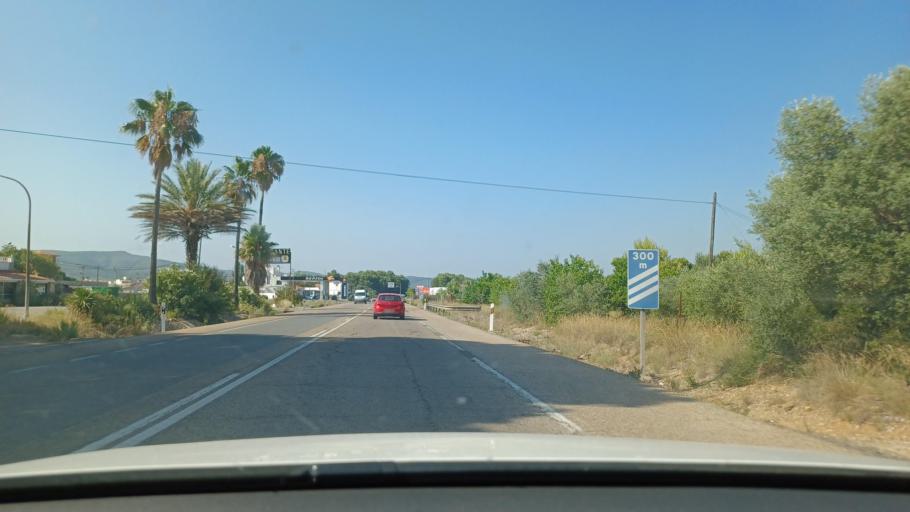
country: ES
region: Valencia
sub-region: Provincia de Castello
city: Alcala de Xivert
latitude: 40.2942
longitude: 0.2263
